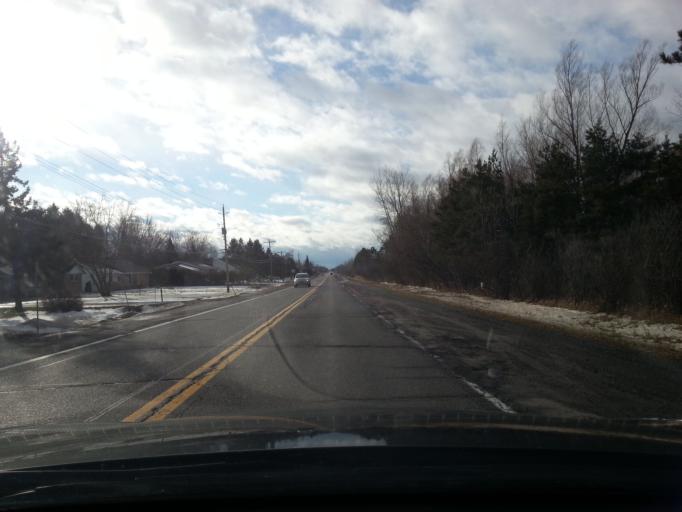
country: CA
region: Ontario
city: Ottawa
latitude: 45.2735
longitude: -75.5850
